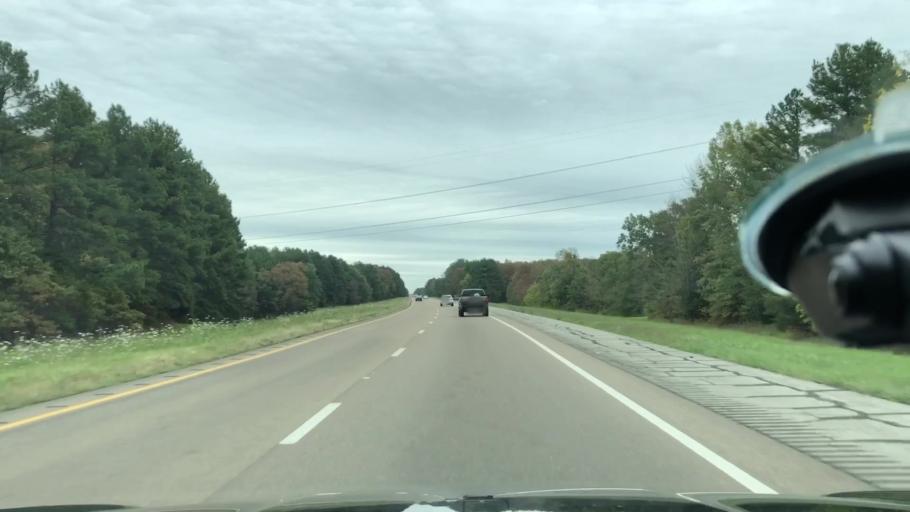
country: US
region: Texas
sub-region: Morris County
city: Naples
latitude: 33.3012
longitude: -94.7081
